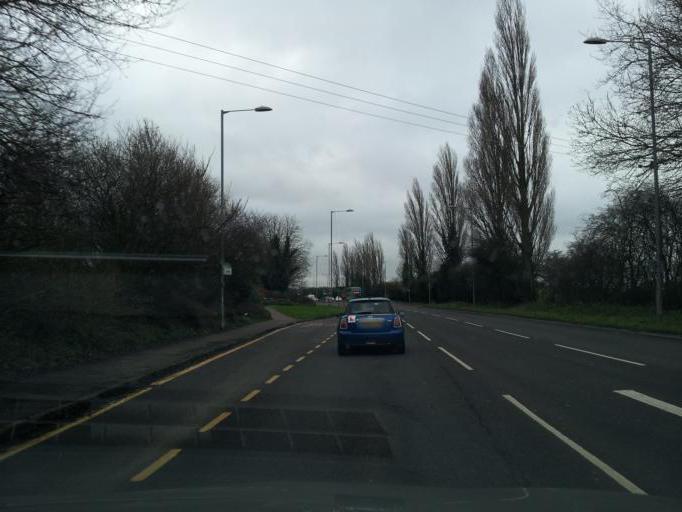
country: GB
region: England
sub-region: Norfolk
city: Cringleford
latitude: 52.5962
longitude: 1.2756
